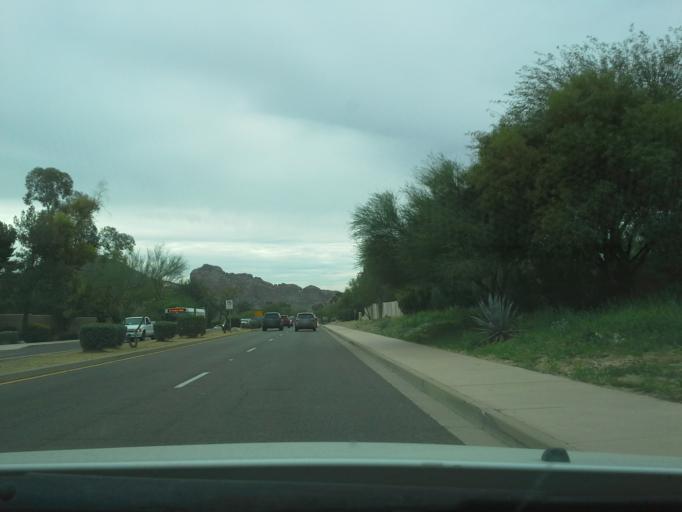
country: US
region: Arizona
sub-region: Maricopa County
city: Paradise Valley
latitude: 33.5511
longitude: -111.9757
